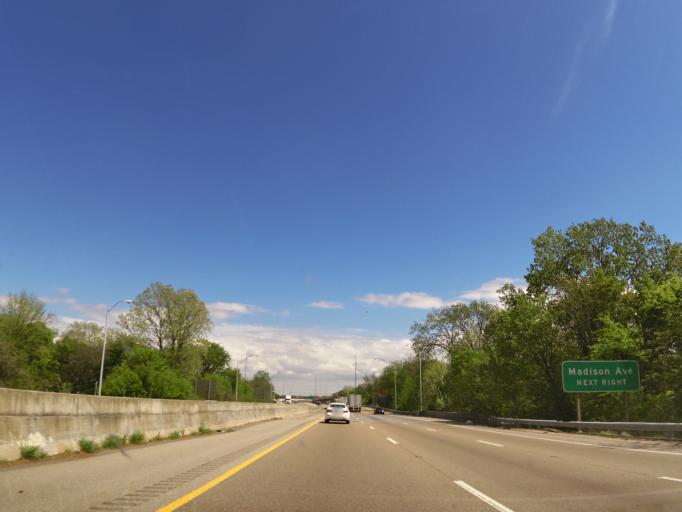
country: US
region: Tennessee
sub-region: Shelby County
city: Memphis
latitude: 35.1504
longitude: -90.0328
